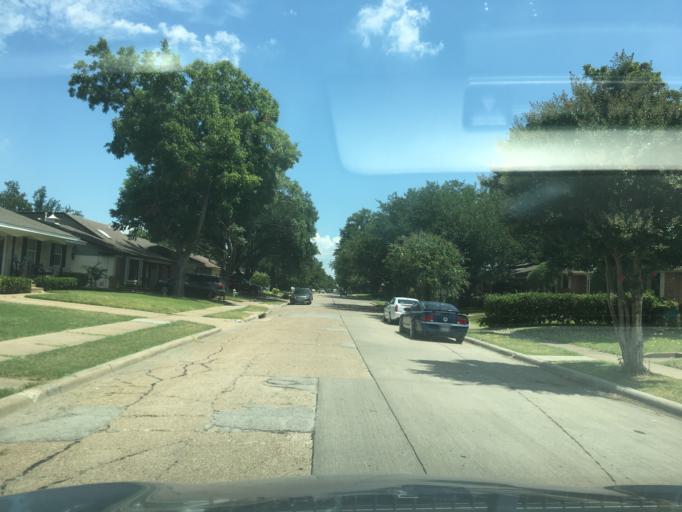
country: US
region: Texas
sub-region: Dallas County
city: Garland
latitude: 32.8712
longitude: -96.6531
